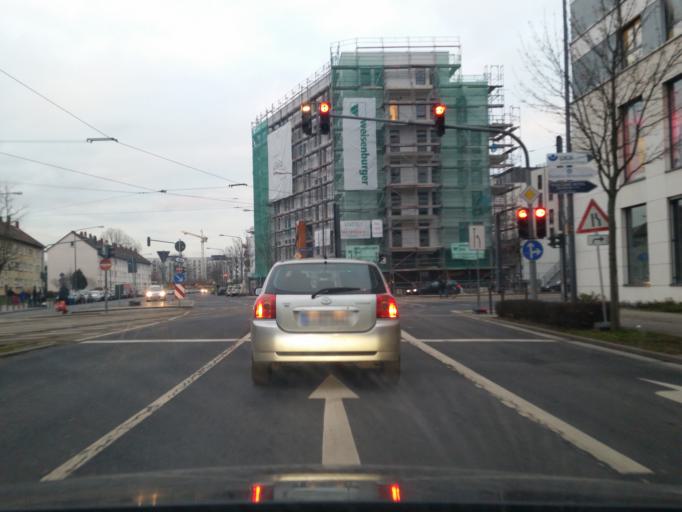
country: DE
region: Hesse
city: Niederrad
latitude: 50.1136
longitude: 8.6277
